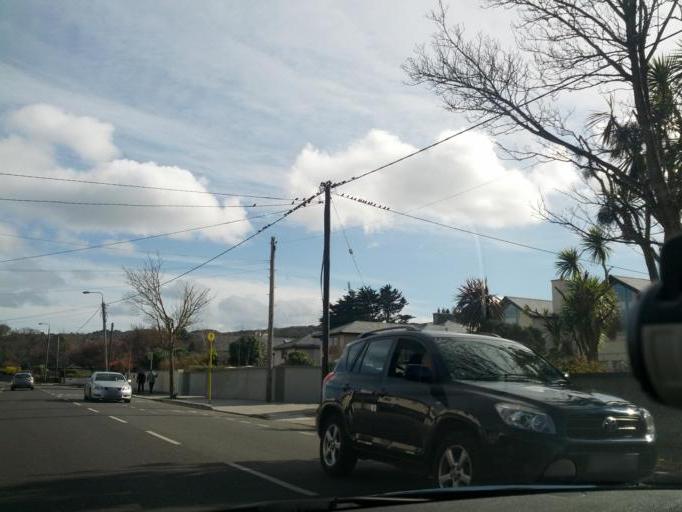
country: IE
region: Leinster
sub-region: Fingal County
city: Howth
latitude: 53.3903
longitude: -6.0842
